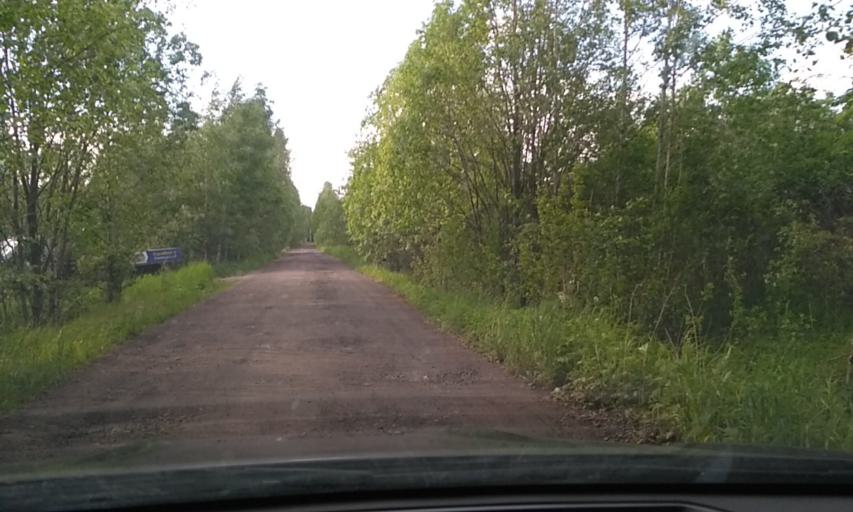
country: RU
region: Leningrad
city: Otradnoye
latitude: 59.8114
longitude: 30.8268
